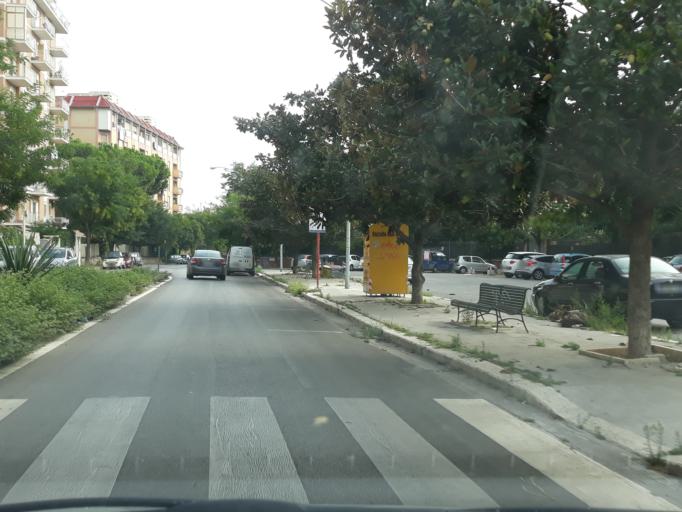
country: IT
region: Sicily
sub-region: Palermo
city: Palermo
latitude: 38.1005
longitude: 13.3269
